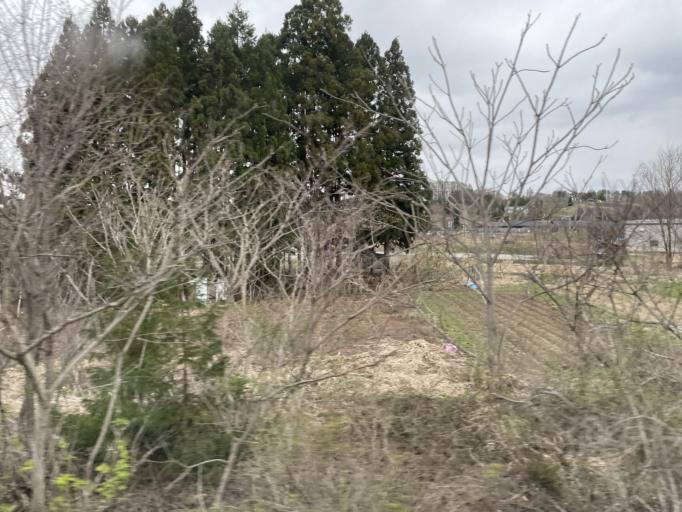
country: JP
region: Aomori
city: Namioka
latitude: 40.7172
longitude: 140.5833
